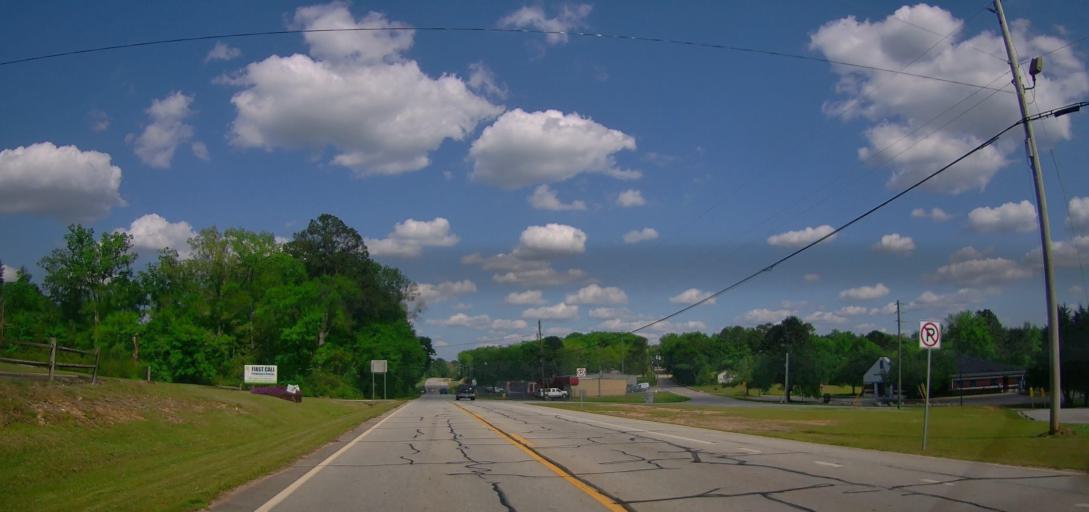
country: US
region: Georgia
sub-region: Greene County
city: Greensboro
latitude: 33.5764
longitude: -83.2002
